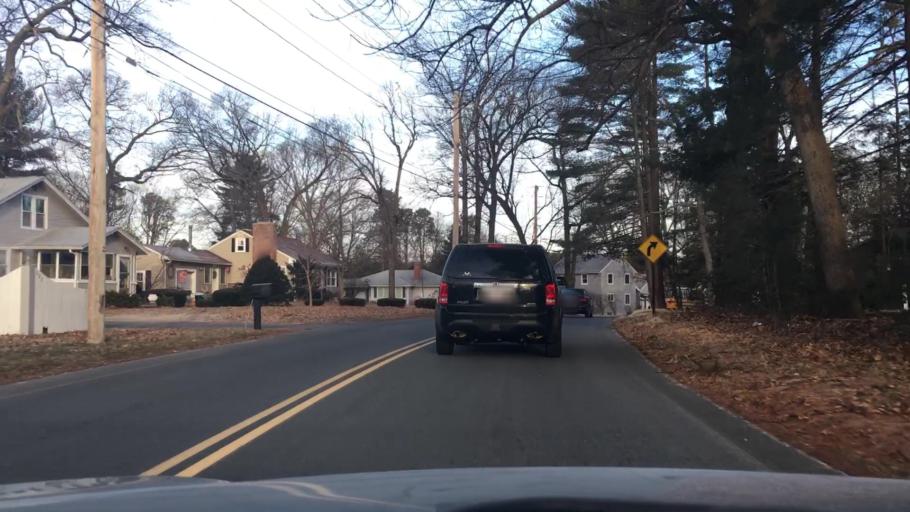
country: US
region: Massachusetts
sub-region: Hampden County
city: Westfield
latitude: 42.1364
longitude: -72.7269
